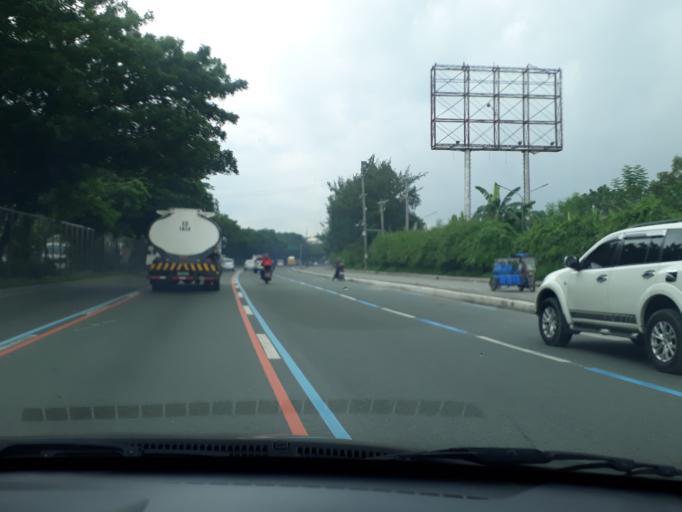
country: PH
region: Calabarzon
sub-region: Province of Rizal
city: Pateros
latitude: 14.5227
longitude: 121.0544
